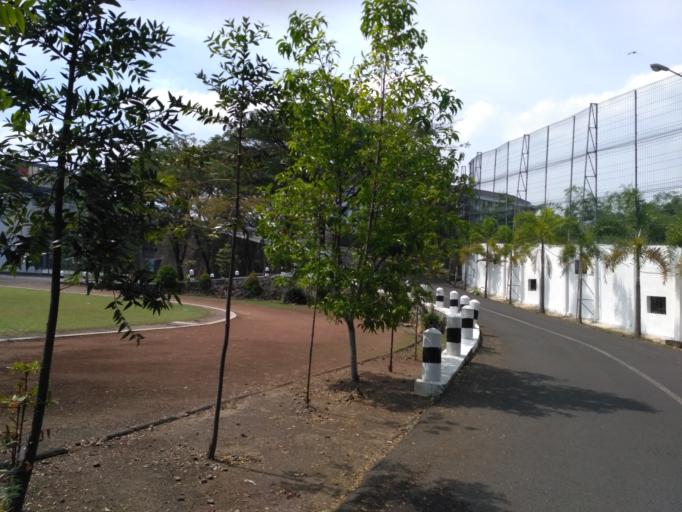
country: ID
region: East Java
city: Malang
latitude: -7.9236
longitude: 112.6008
